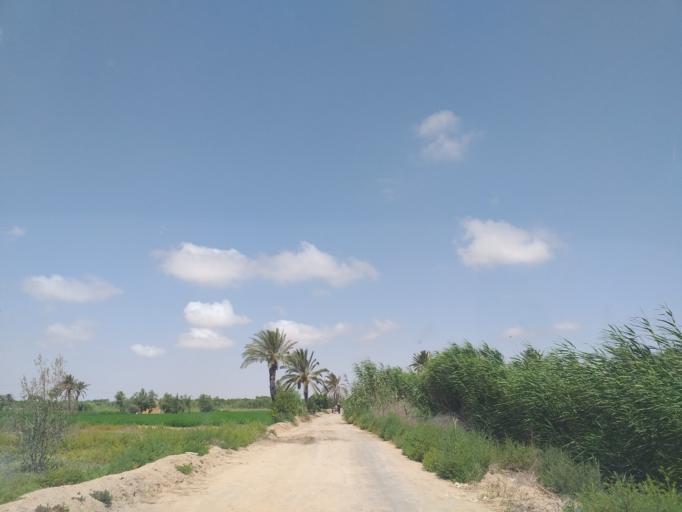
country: TN
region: Qabis
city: Gabes
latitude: 33.9525
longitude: 10.0479
